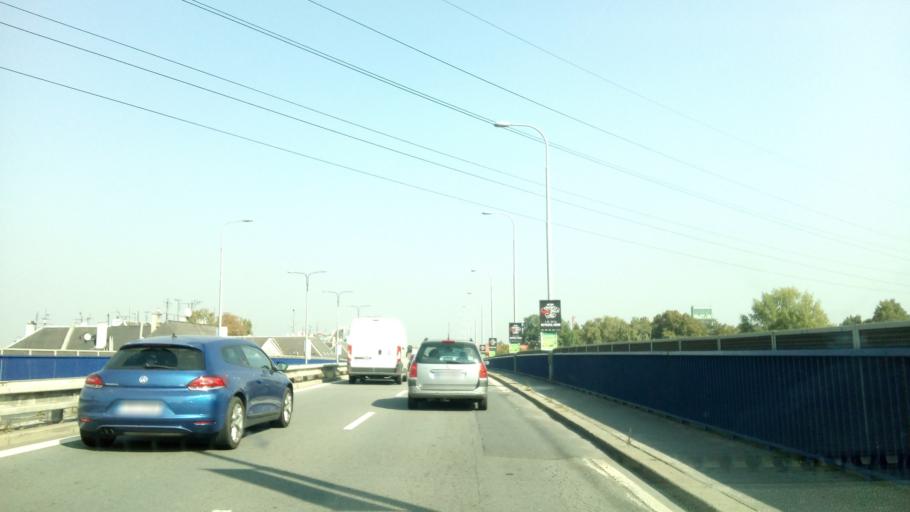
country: CZ
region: Moravskoslezsky
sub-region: Okres Ostrava-Mesto
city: Ostrava
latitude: 49.8033
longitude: 18.2605
